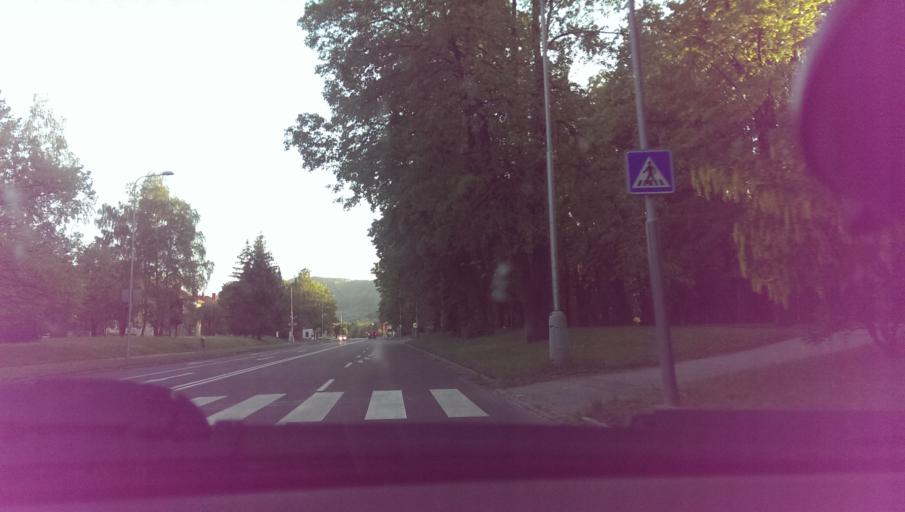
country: CZ
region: Moravskoslezsky
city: Frenstat pod Radhostem
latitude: 49.5435
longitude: 18.2089
